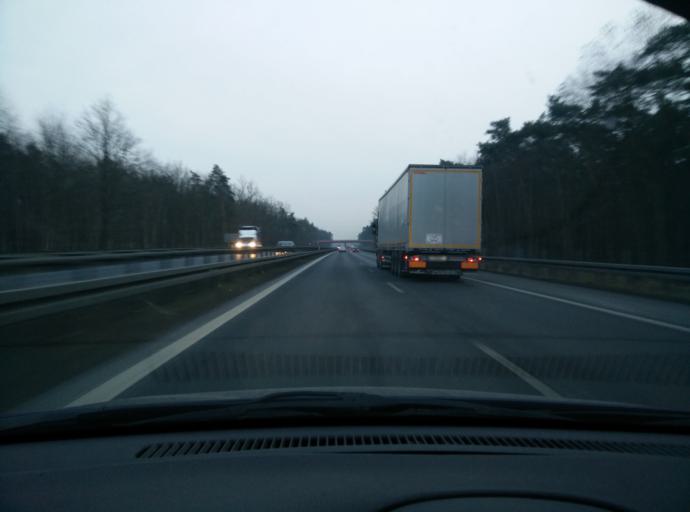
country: PL
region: Greater Poland Voivodeship
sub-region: Powiat poznanski
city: Kornik
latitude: 52.2806
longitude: 17.0615
